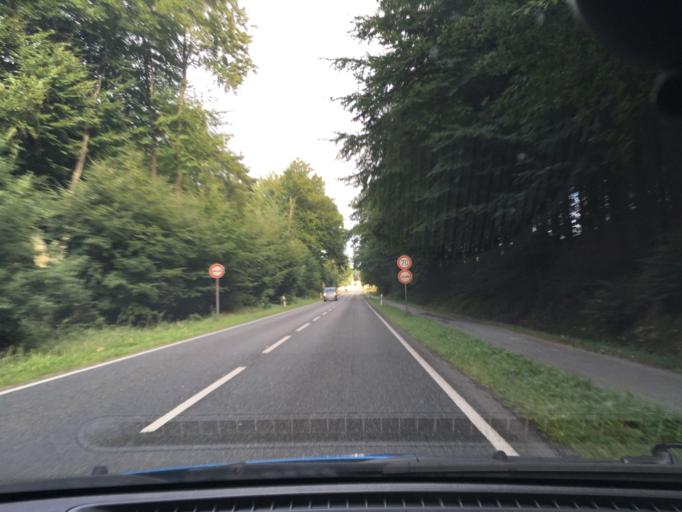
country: DE
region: Lower Saxony
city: Buchholz in der Nordheide
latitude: 53.4043
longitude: 9.8745
